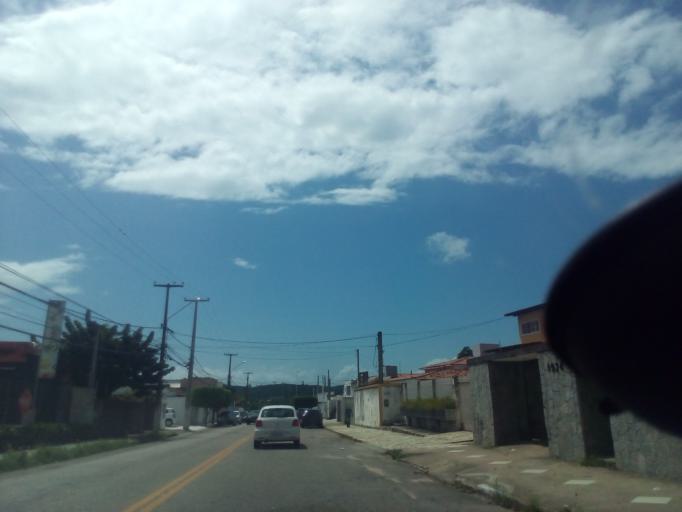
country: BR
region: Rio Grande do Norte
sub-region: Natal
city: Natal
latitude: -5.8385
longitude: -35.2130
